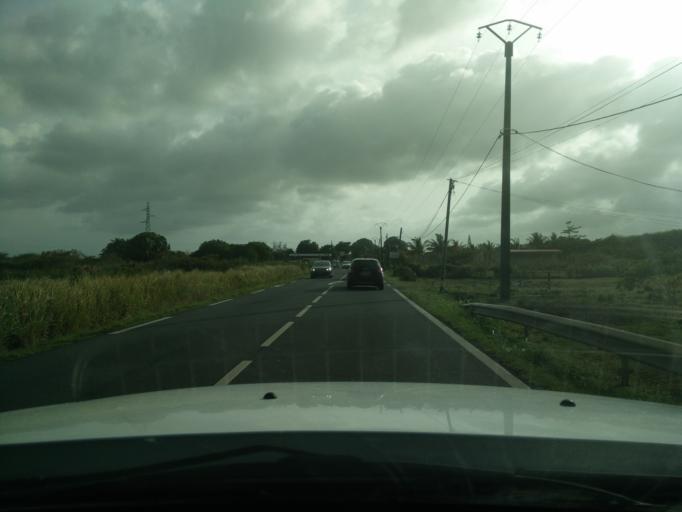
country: GP
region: Guadeloupe
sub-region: Guadeloupe
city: Saint-Francois
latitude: 16.2577
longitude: -61.3067
